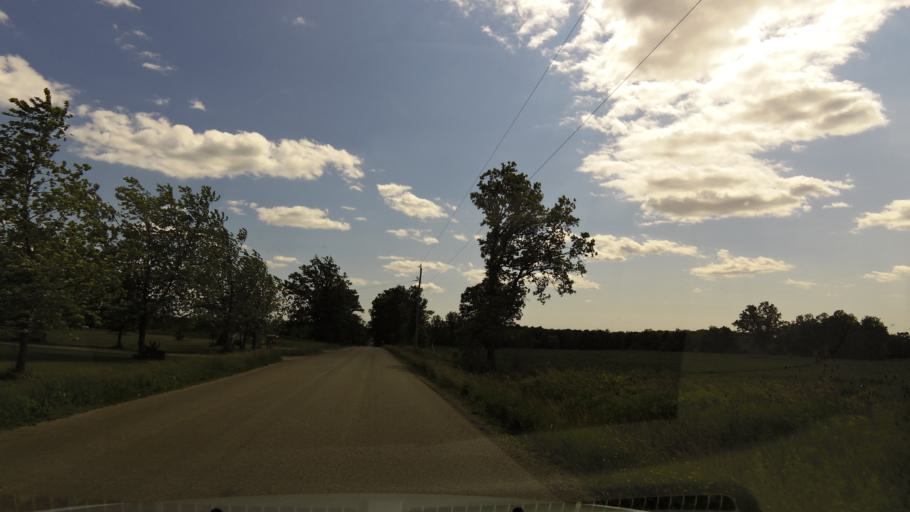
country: CA
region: Ontario
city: Ancaster
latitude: 43.1330
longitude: -80.0795
